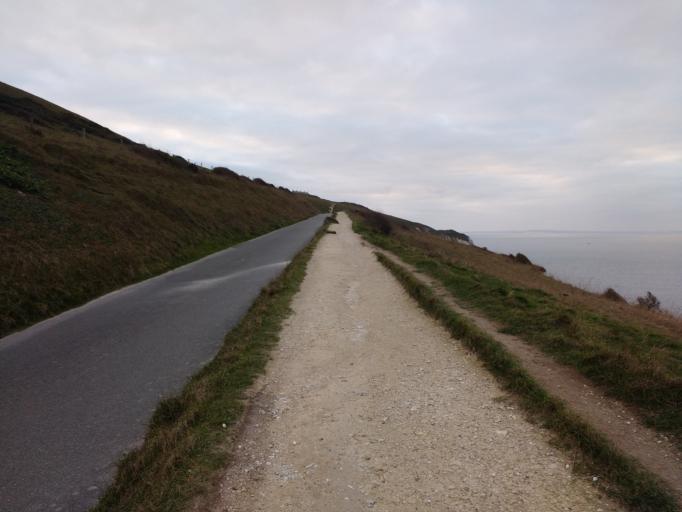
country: GB
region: England
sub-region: Isle of Wight
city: Totland
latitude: 50.6656
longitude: -1.5674
